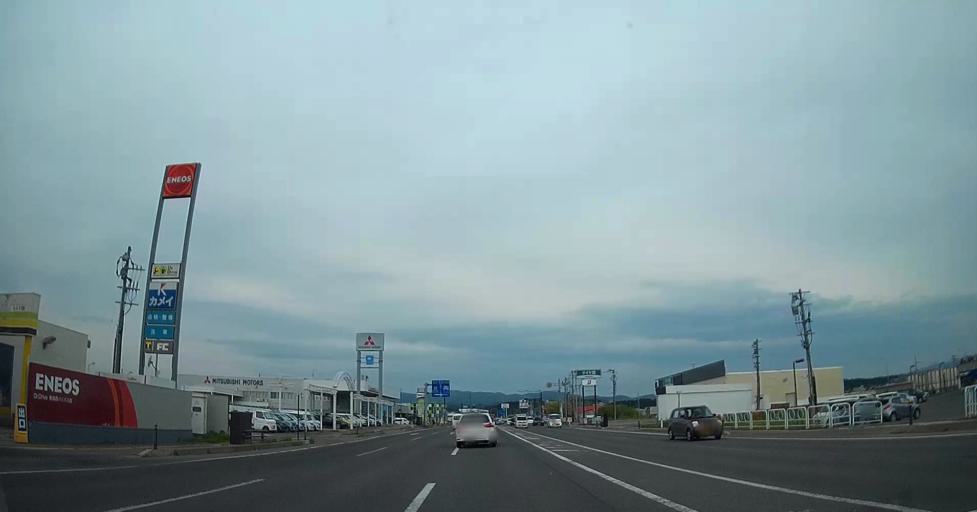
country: JP
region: Aomori
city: Aomori Shi
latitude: 40.8336
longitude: 140.6917
